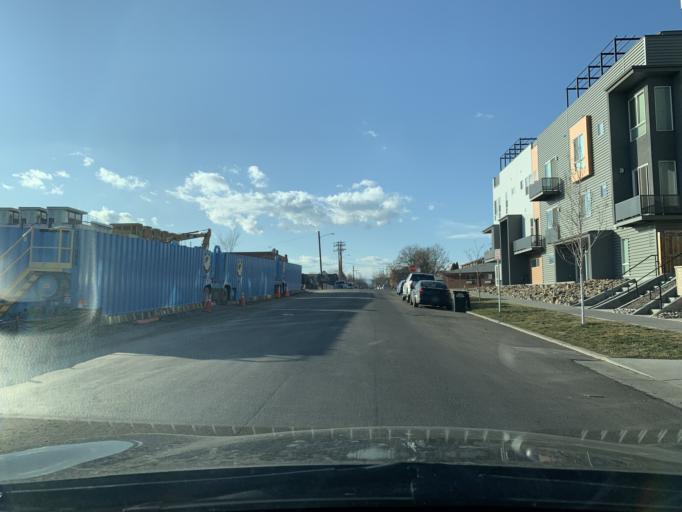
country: US
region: Colorado
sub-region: Jefferson County
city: Edgewater
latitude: 39.7427
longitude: -105.0260
